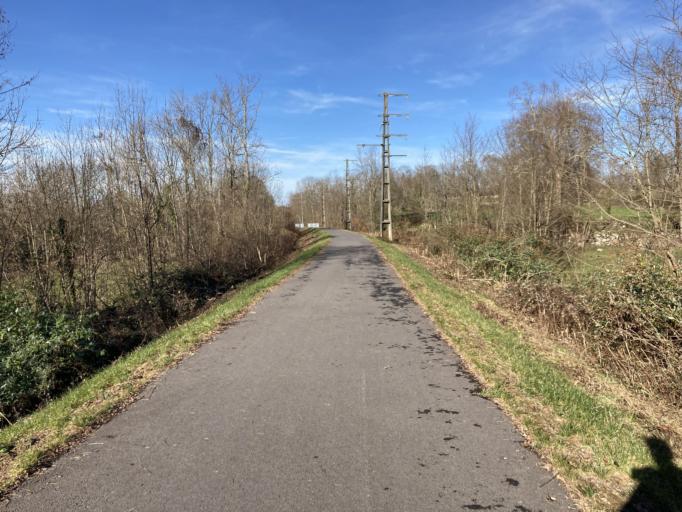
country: FR
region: Aquitaine
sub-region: Departement des Pyrenees-Atlantiques
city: Arudy
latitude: 43.1324
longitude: -0.4448
